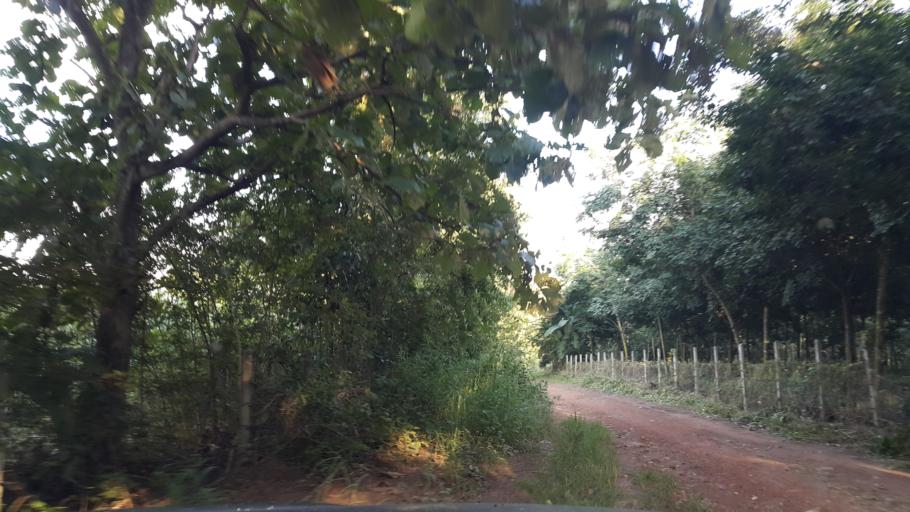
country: TH
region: Chiang Mai
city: Mae On
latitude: 18.7441
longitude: 99.2454
